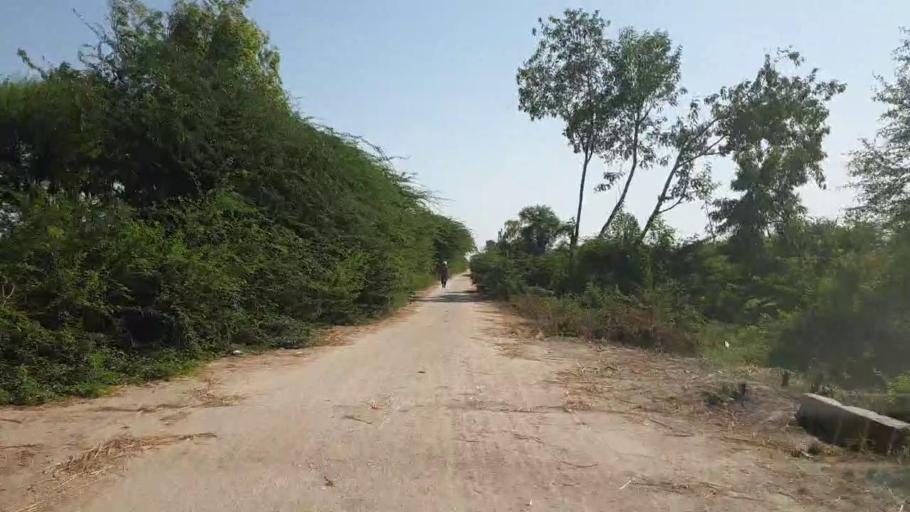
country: PK
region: Sindh
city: Tando Bago
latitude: 24.6567
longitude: 68.9801
